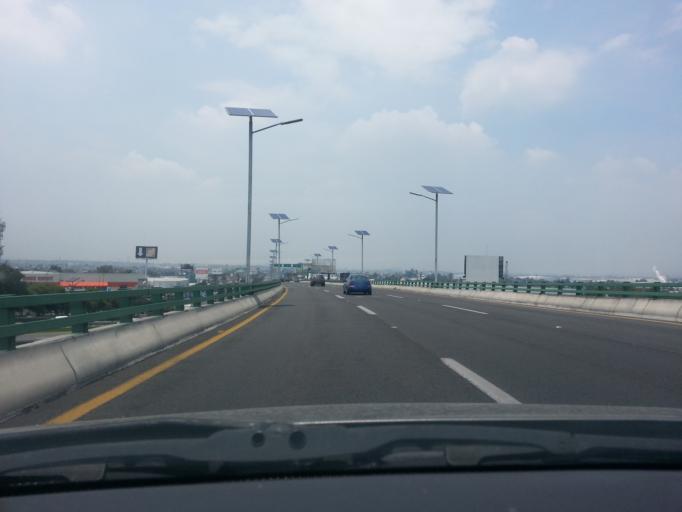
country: MX
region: Mexico
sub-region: Tultitlan
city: Buenavista
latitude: 19.6017
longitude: -99.1886
